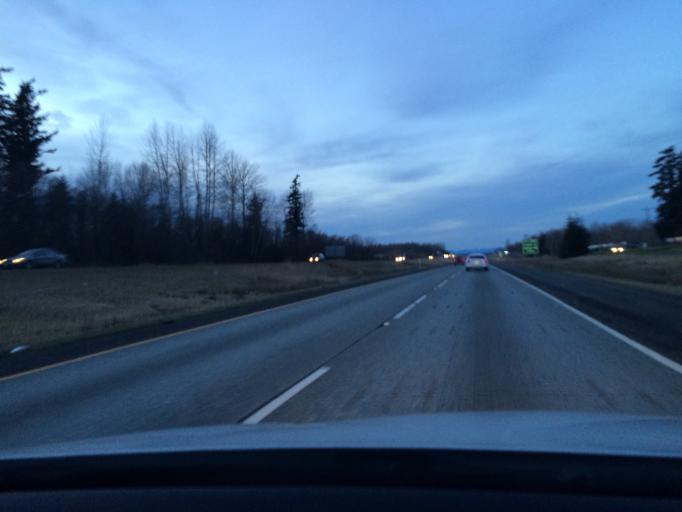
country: US
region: Washington
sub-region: Whatcom County
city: Marietta-Alderwood
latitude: 48.8009
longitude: -122.5320
